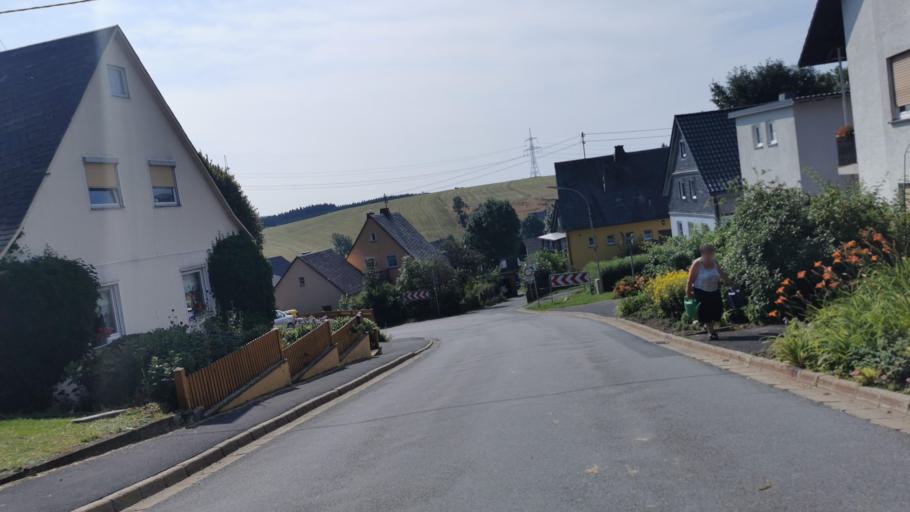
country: DE
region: Bavaria
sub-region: Upper Franconia
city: Tschirn
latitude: 50.3981
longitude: 11.4481
